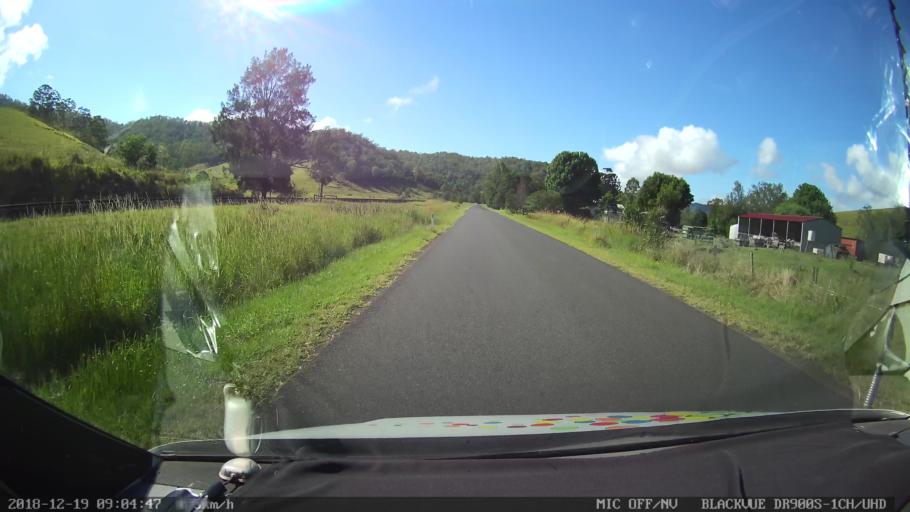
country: AU
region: New South Wales
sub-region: Kyogle
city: Kyogle
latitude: -28.4579
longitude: 152.9445
